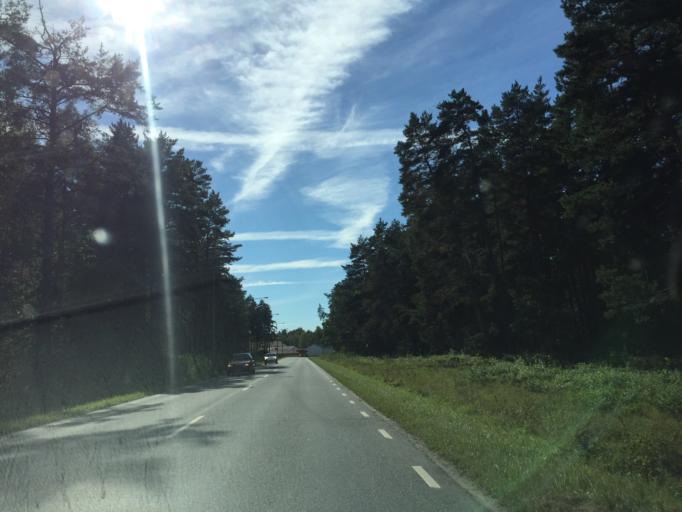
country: SE
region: OErebro
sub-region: Orebro Kommun
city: Orebro
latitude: 59.2900
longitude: 15.2460
